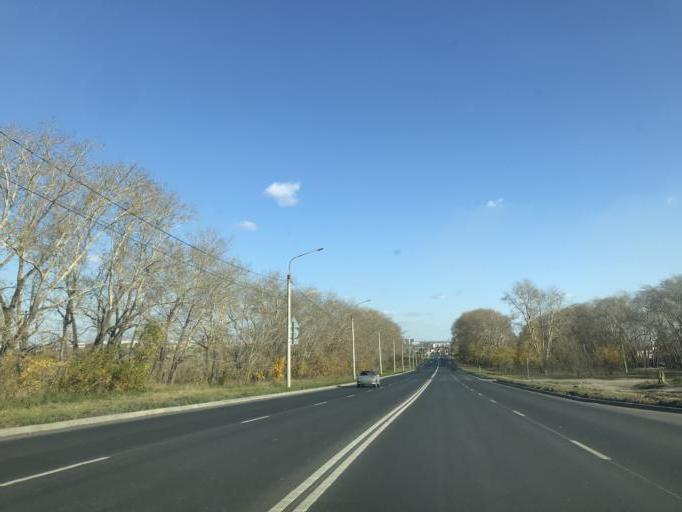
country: RU
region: Chelyabinsk
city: Roshchino
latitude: 55.2402
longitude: 61.3342
